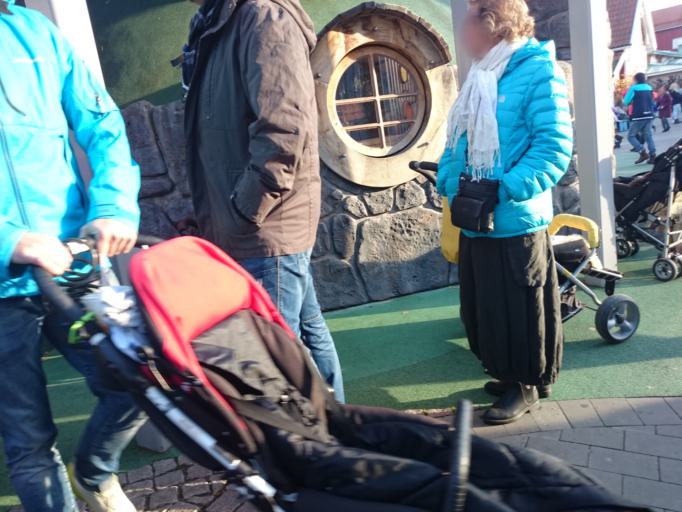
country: SE
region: Vaestra Goetaland
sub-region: Goteborg
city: Goeteborg
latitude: 57.6958
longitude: 11.9942
